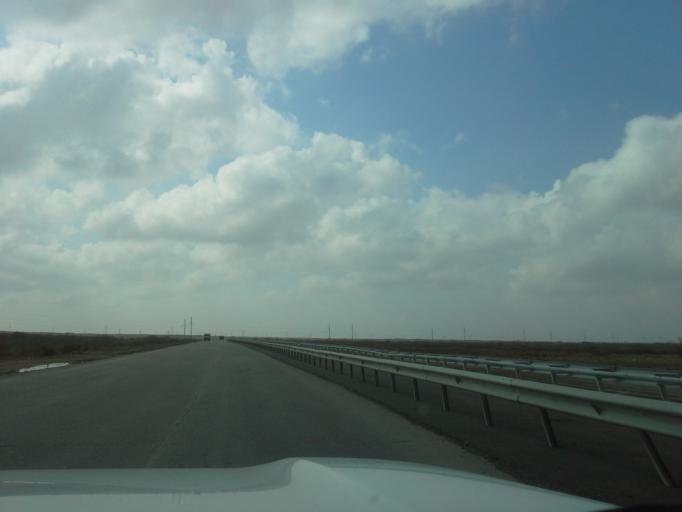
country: TM
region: Mary
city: Mary
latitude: 37.3463
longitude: 61.4299
